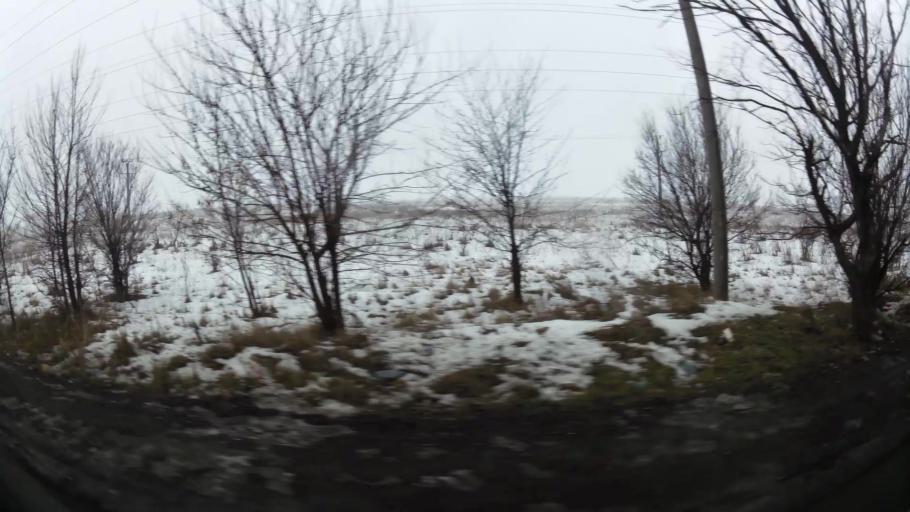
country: RO
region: Ilfov
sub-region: Comuna Chiajna
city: Chiajna
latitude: 44.4269
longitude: 25.9675
